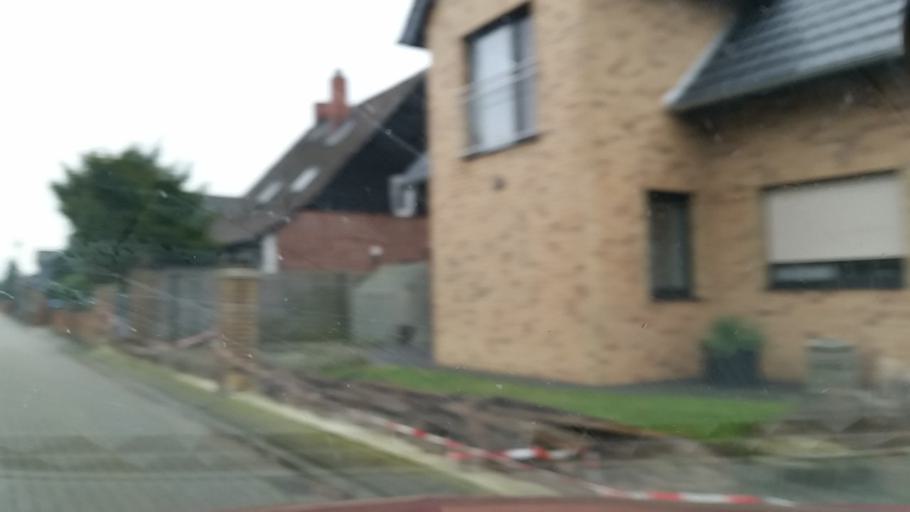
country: DE
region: Lower Saxony
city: Wolfsburg
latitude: 52.4466
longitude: 10.7739
